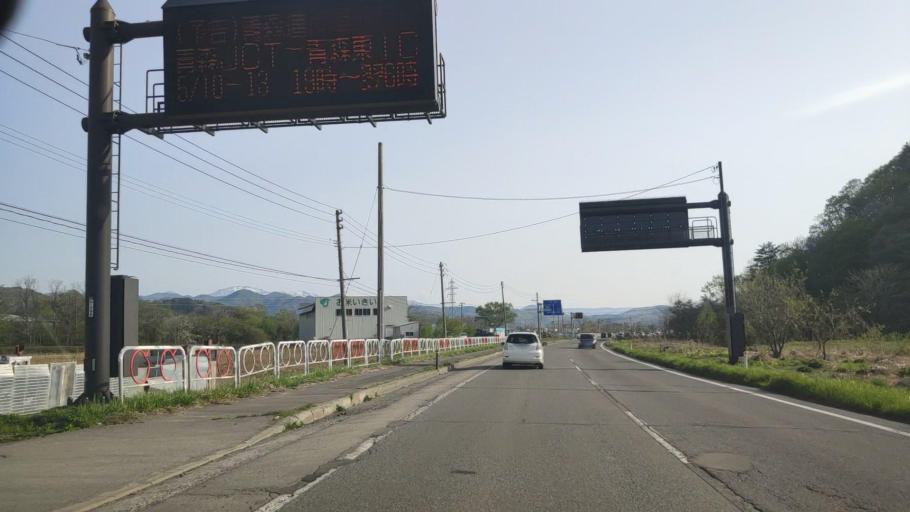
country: JP
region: Aomori
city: Aomori Shi
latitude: 40.8500
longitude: 140.8380
